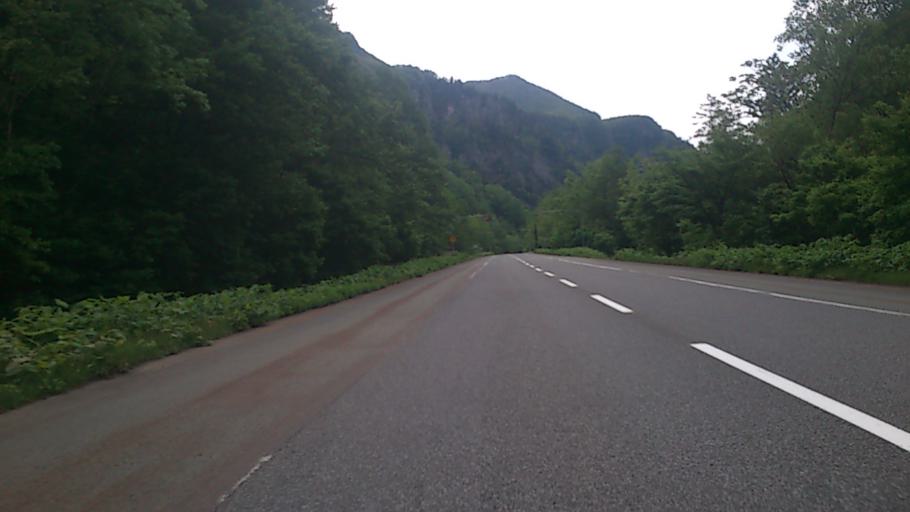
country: JP
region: Hokkaido
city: Kamikawa
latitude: 43.7557
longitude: 142.9266
